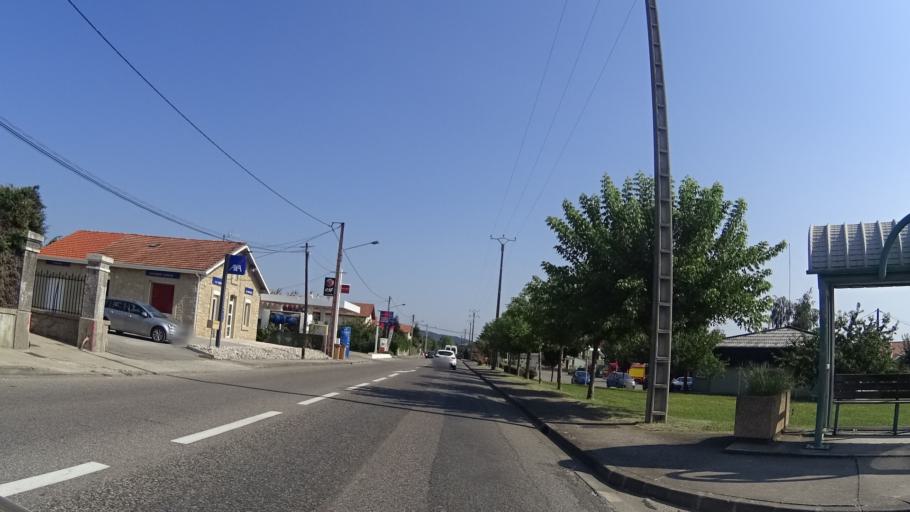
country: FR
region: Midi-Pyrenees
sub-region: Departement de l'Ariege
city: Lavelanet
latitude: 42.9728
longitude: 1.8671
